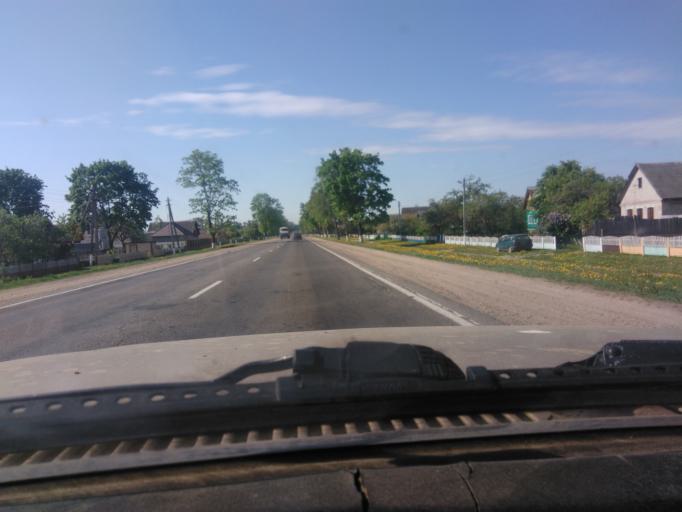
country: BY
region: Mogilev
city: Buynichy
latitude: 53.8352
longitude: 30.2459
